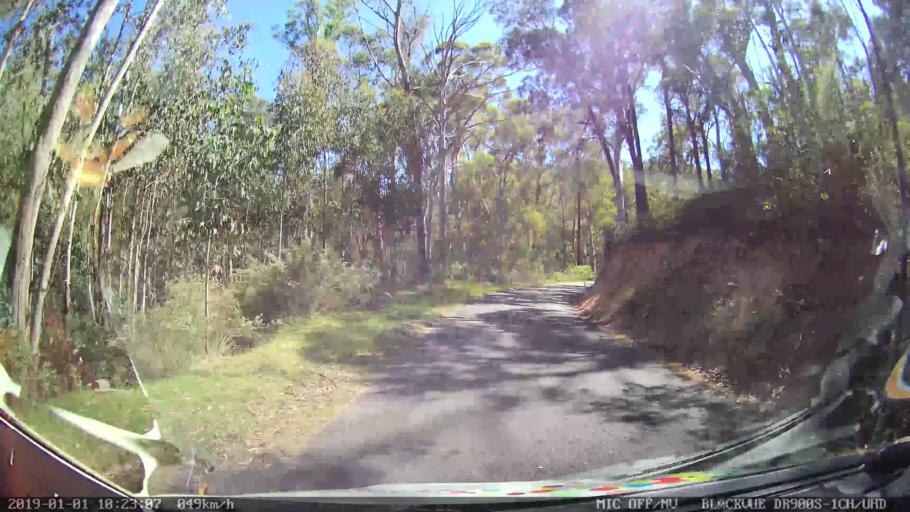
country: AU
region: New South Wales
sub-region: Snowy River
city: Jindabyne
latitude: -36.0758
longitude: 148.2092
